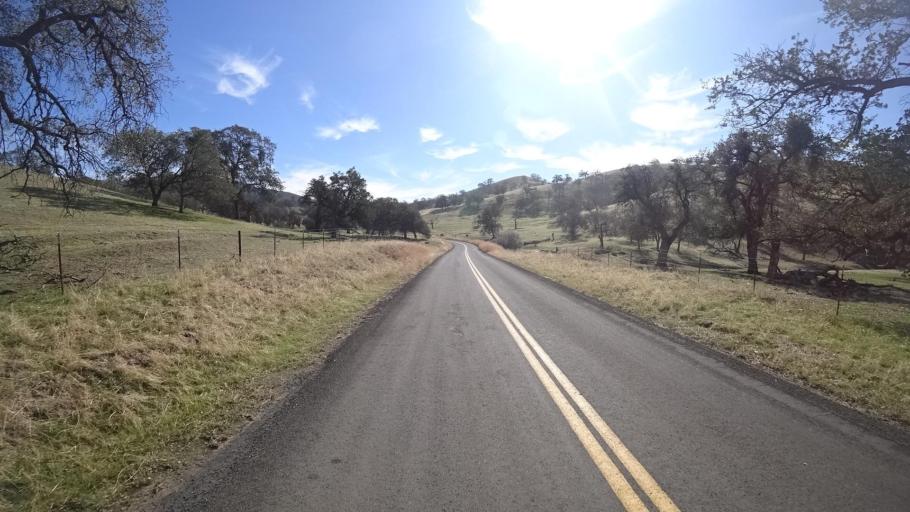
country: US
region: California
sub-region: Tulare County
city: Richgrove
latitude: 35.6719
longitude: -118.8521
